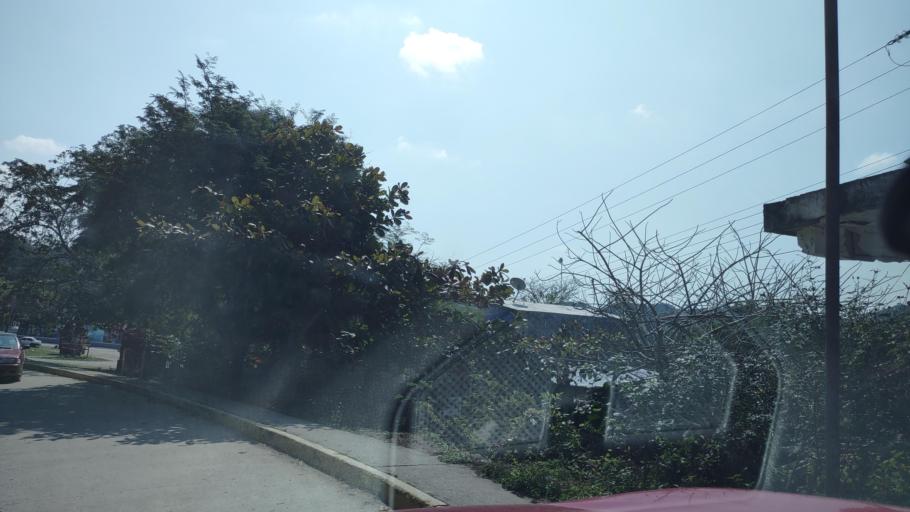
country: MX
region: Veracruz
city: Agua Dulce
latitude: 20.3129
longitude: -97.1743
